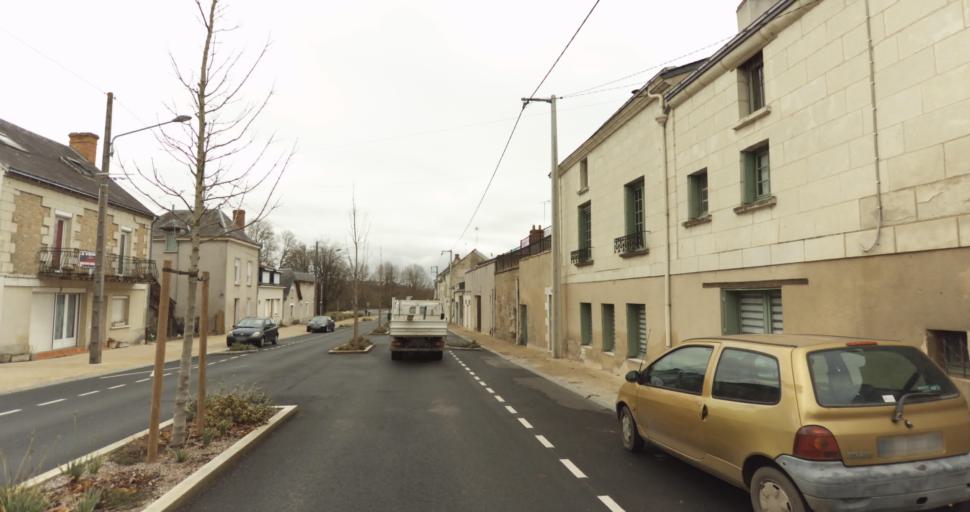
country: FR
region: Pays de la Loire
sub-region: Departement de Maine-et-Loire
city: Montreuil-Bellay
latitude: 47.1382
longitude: -0.1556
